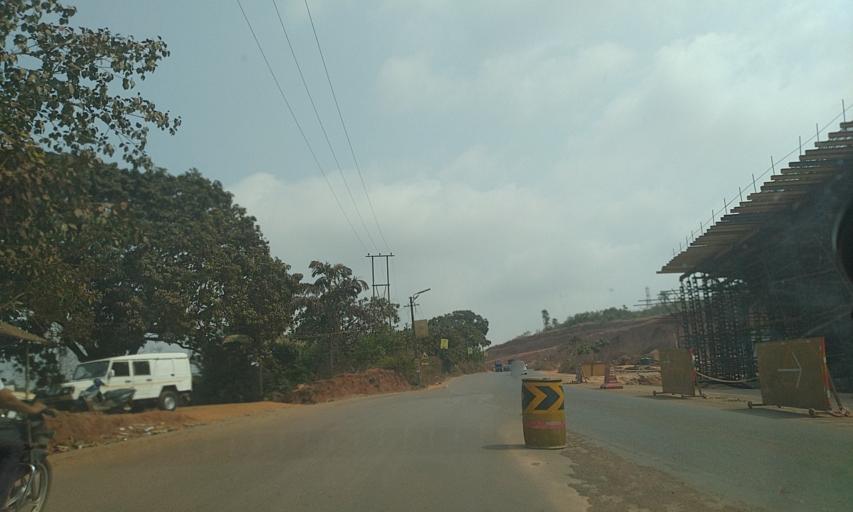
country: IN
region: Goa
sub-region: South Goa
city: Sancoale
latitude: 15.3867
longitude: 73.9209
